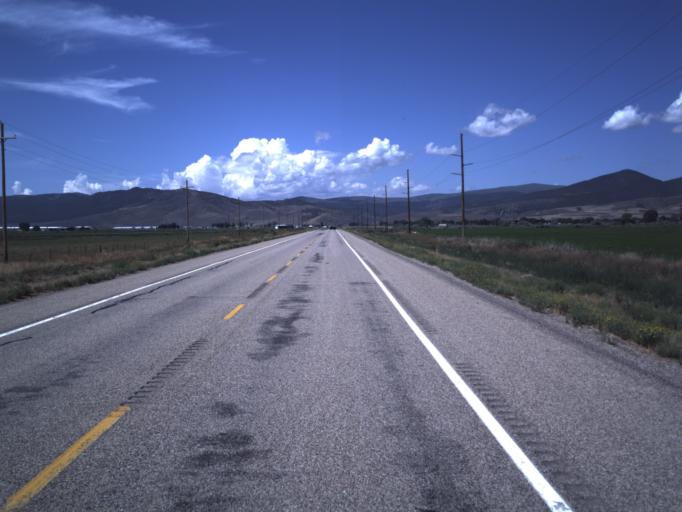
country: US
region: Utah
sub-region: Piute County
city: Junction
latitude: 38.1841
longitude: -112.2446
